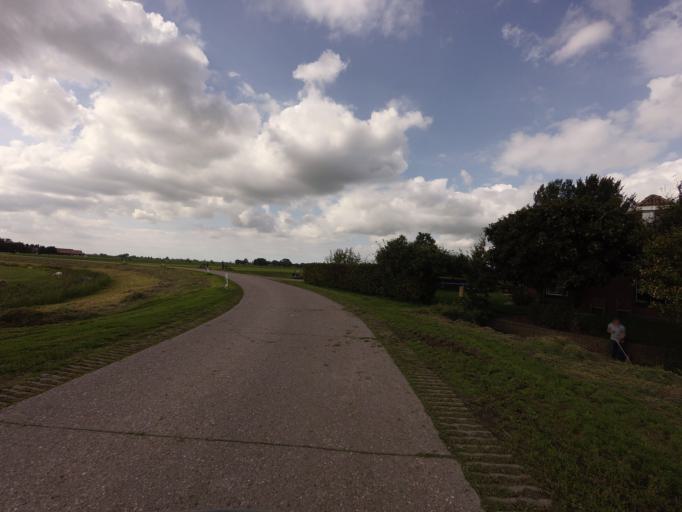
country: NL
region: Friesland
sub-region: Gemeente Littenseradiel
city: Wommels
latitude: 53.0749
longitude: 5.6182
